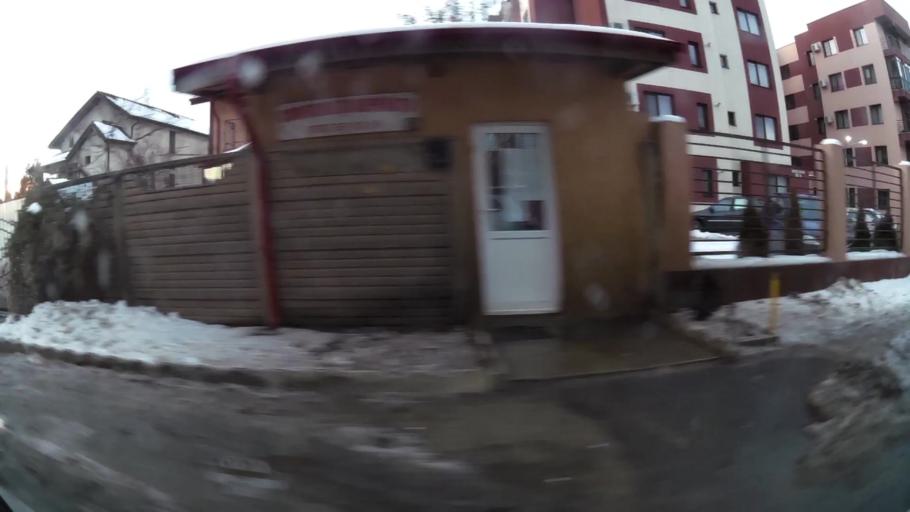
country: RO
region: Ilfov
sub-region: Comuna Popesti-Leordeni
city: Popesti-Leordeni
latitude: 44.3677
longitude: 26.1513
